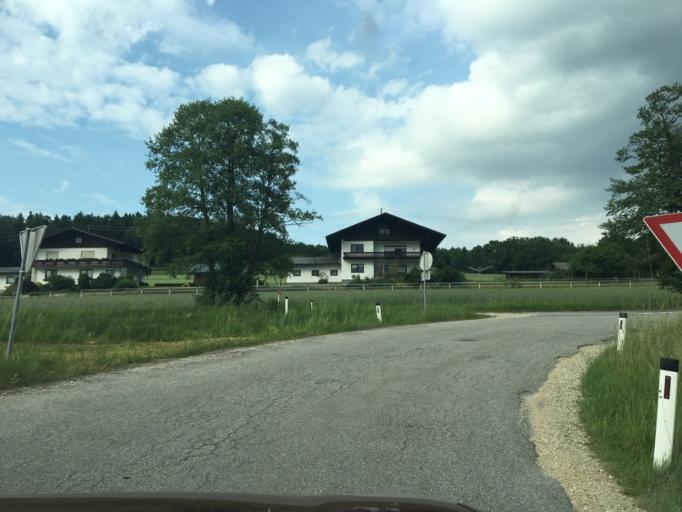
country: AT
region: Upper Austria
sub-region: Politischer Bezirk Braunau am Inn
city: Altheim
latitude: 48.1308
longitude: 13.2189
